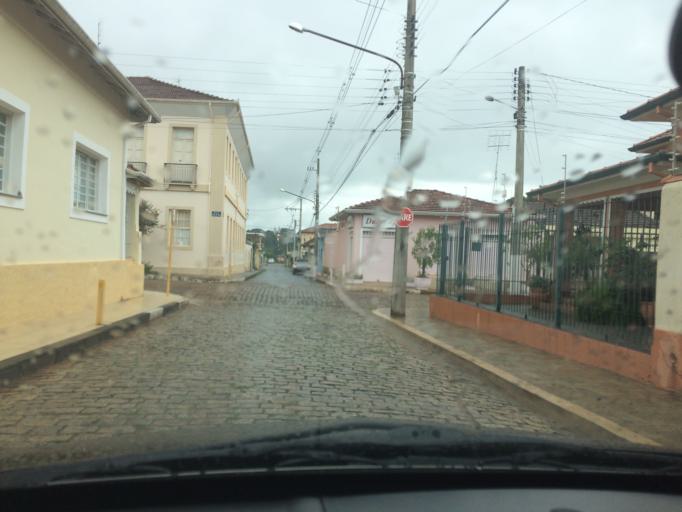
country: BR
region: Sao Paulo
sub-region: Casa Branca
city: Casa Branca
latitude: -21.7715
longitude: -47.0885
